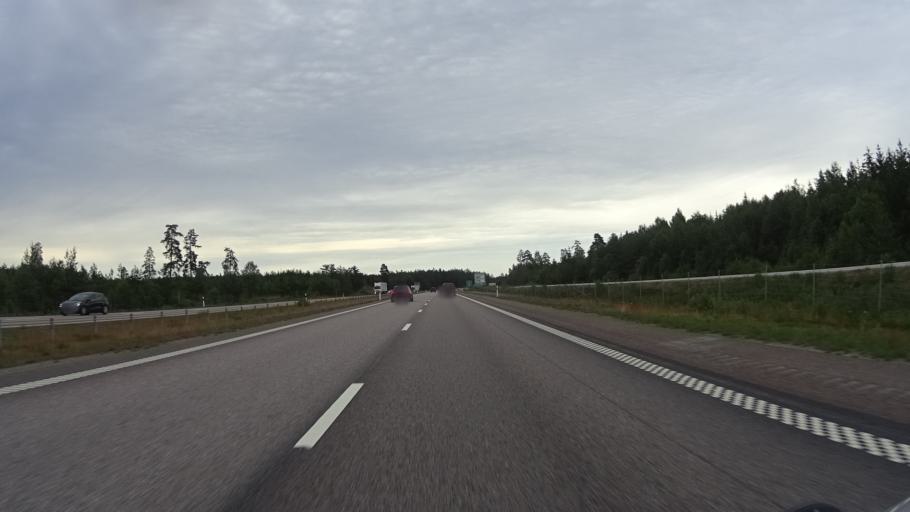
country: SE
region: OEstergoetland
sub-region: Norrkopings Kommun
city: Krokek
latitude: 58.7151
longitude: 16.3700
